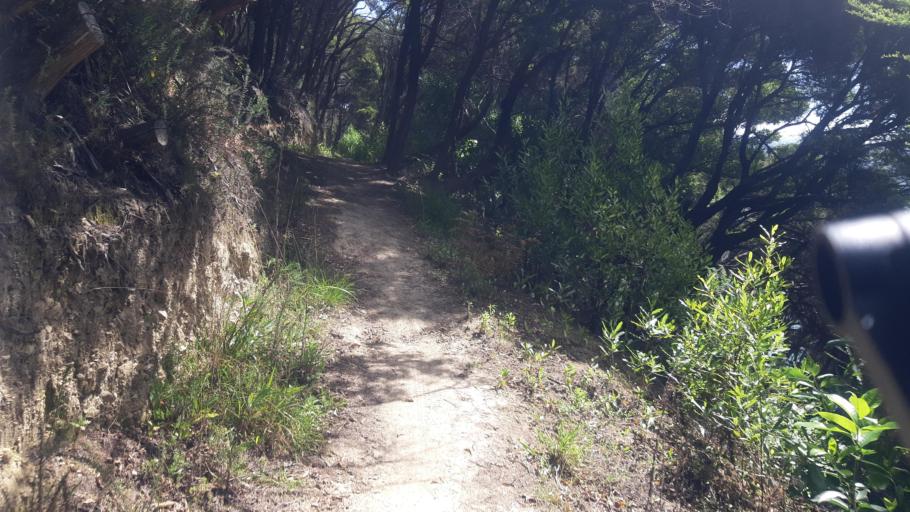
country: NZ
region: Marlborough
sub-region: Marlborough District
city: Picton
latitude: -41.2547
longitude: 174.0402
